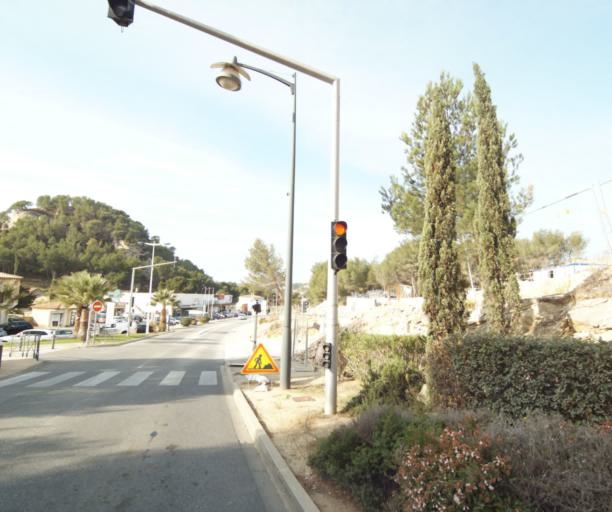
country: FR
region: Provence-Alpes-Cote d'Azur
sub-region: Departement des Bouches-du-Rhone
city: Ensues-la-Redonne
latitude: 43.3556
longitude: 5.1976
